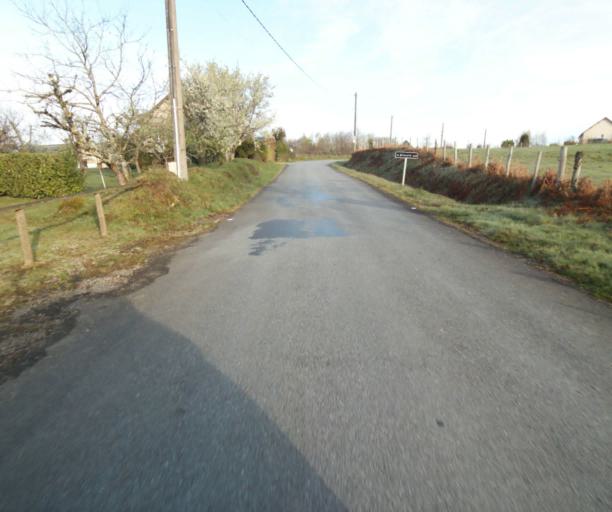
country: FR
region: Limousin
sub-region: Departement de la Correze
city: Naves
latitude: 45.3142
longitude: 1.8346
